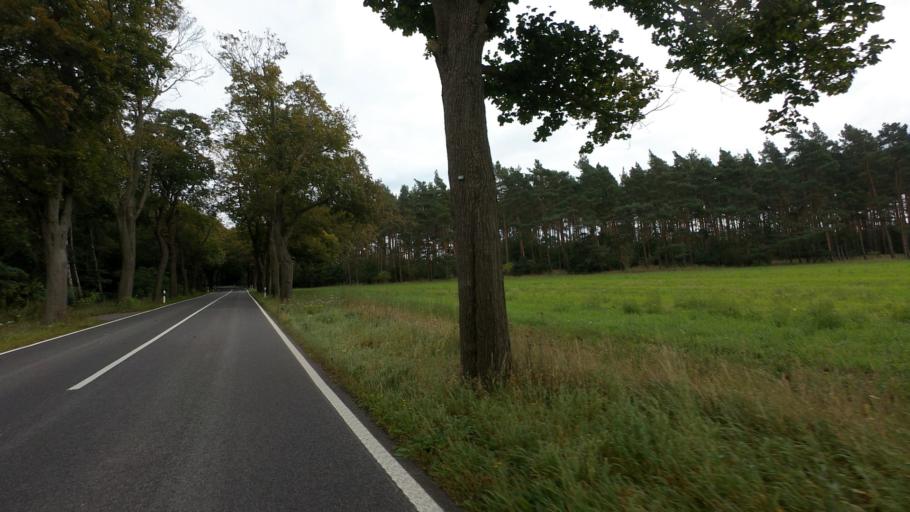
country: DE
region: Brandenburg
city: Baruth
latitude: 52.0391
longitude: 13.4942
